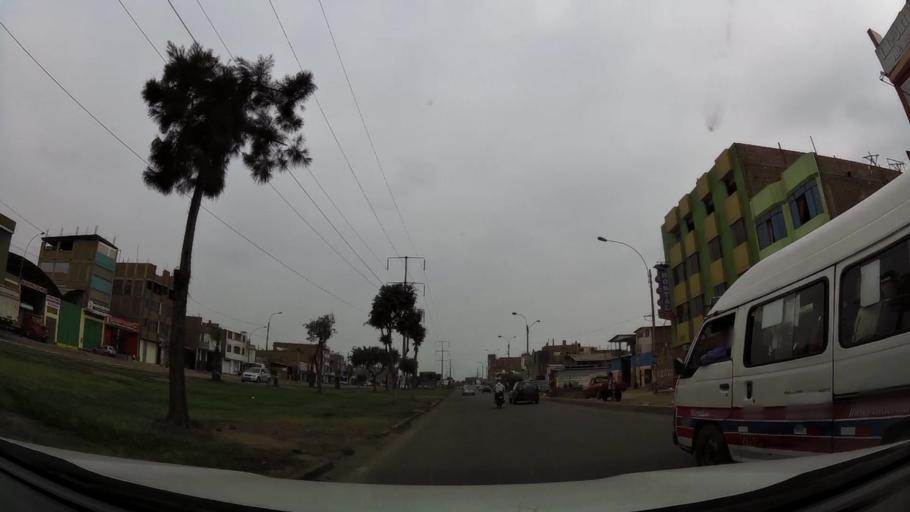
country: PE
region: Lima
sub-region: Lima
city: Independencia
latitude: -11.9868
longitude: -77.0801
